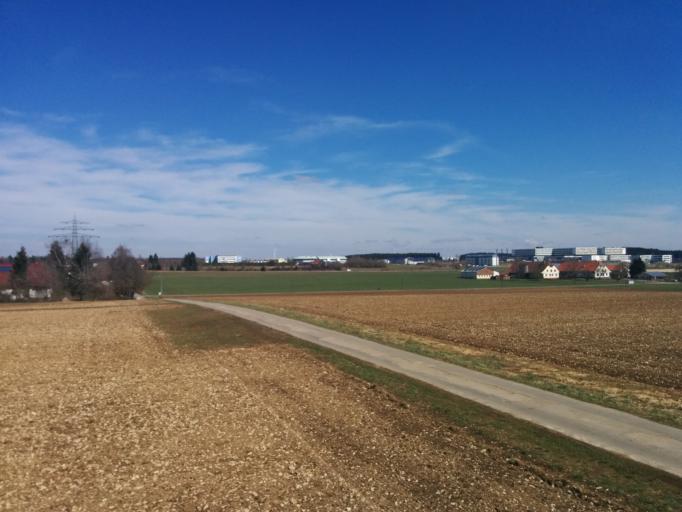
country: DE
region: Baden-Wuerttemberg
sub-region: Freiburg Region
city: Villingen-Schwenningen
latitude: 48.0561
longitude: 8.4873
